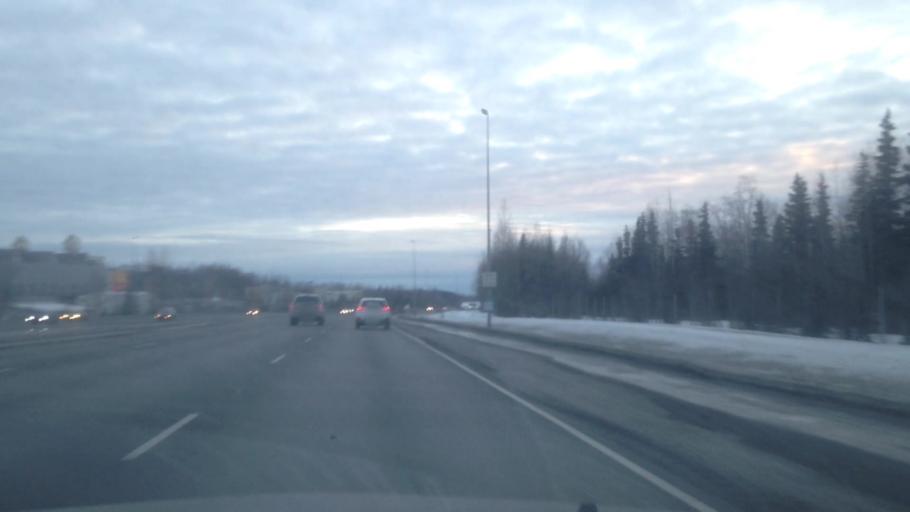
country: US
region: Alaska
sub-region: Anchorage Municipality
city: Elmendorf Air Force Base
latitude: 61.2333
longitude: -149.7094
